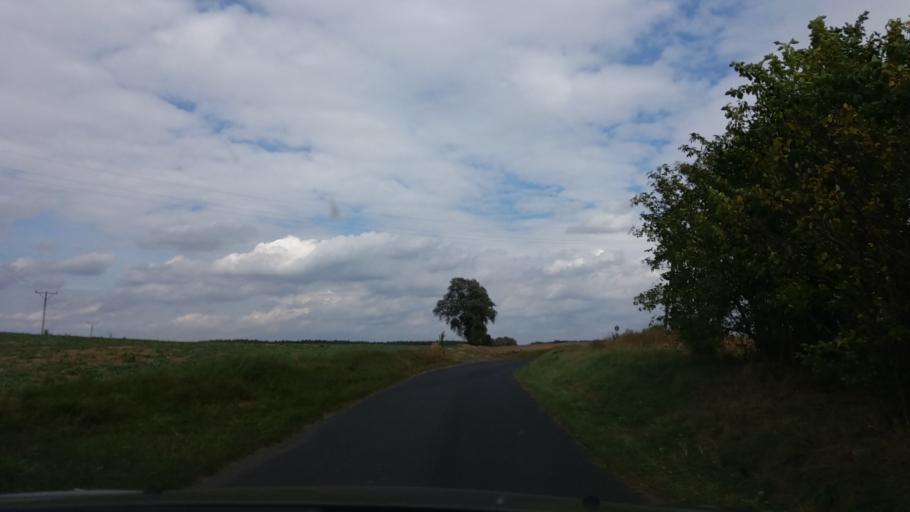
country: PL
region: West Pomeranian Voivodeship
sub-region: Powiat stargardzki
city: Kobylanka
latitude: 53.3254
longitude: 14.8610
